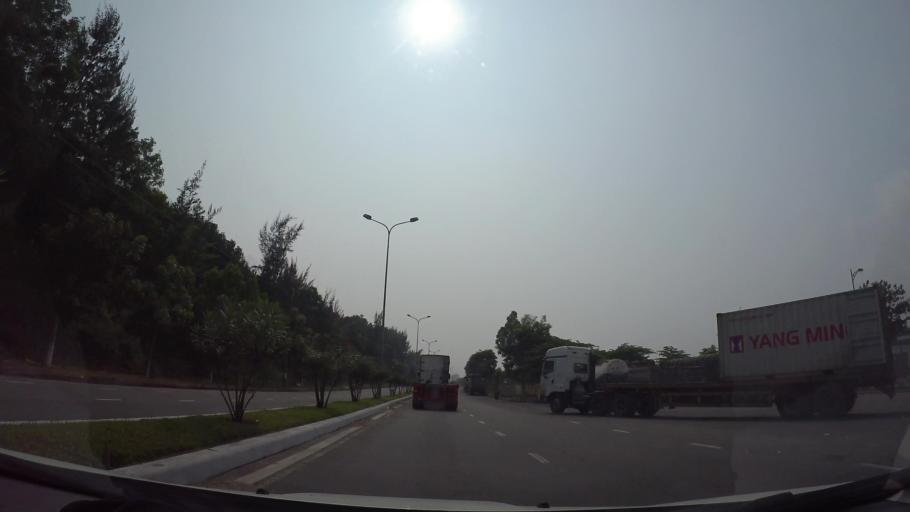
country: VN
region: Da Nang
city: Da Nang
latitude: 16.1162
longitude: 108.2327
